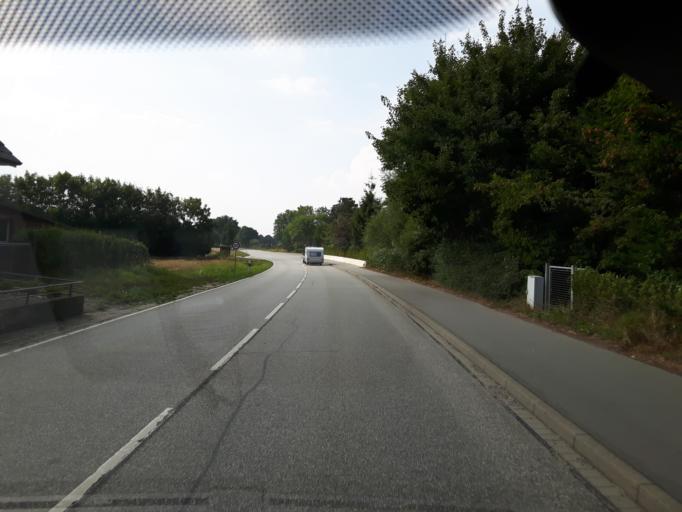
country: DE
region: Schleswig-Holstein
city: Goosefeld
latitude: 54.4418
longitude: 9.8194
